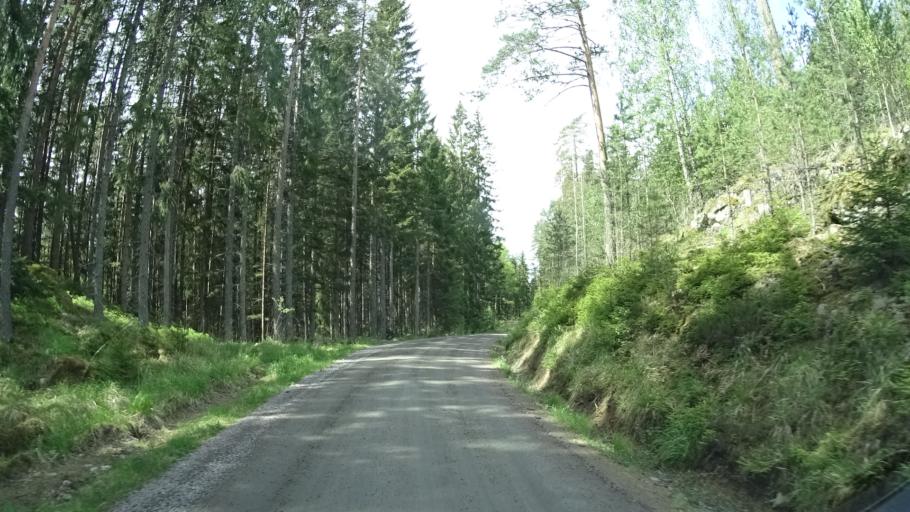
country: SE
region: OEstergoetland
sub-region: Finspangs Kommun
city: Finspang
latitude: 58.7658
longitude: 15.8428
